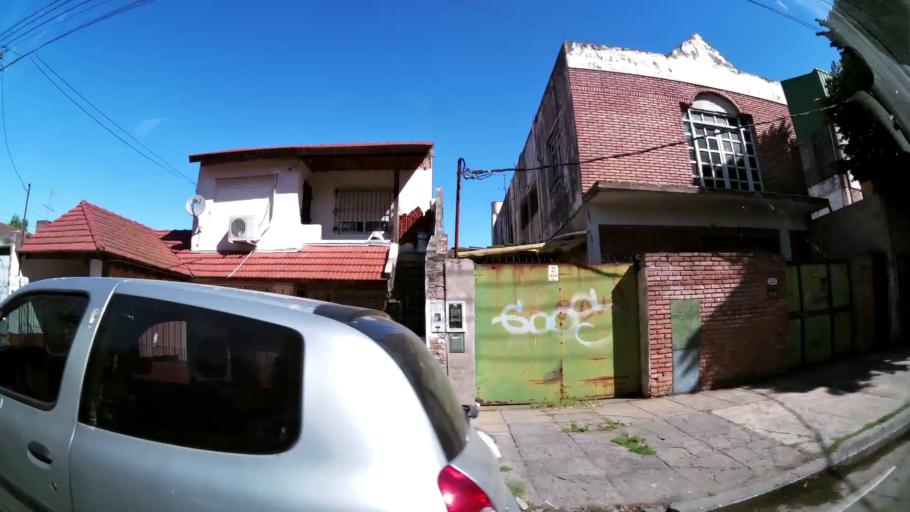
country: AR
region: Buenos Aires
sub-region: Partido de San Isidro
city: San Isidro
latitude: -34.4619
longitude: -58.5409
